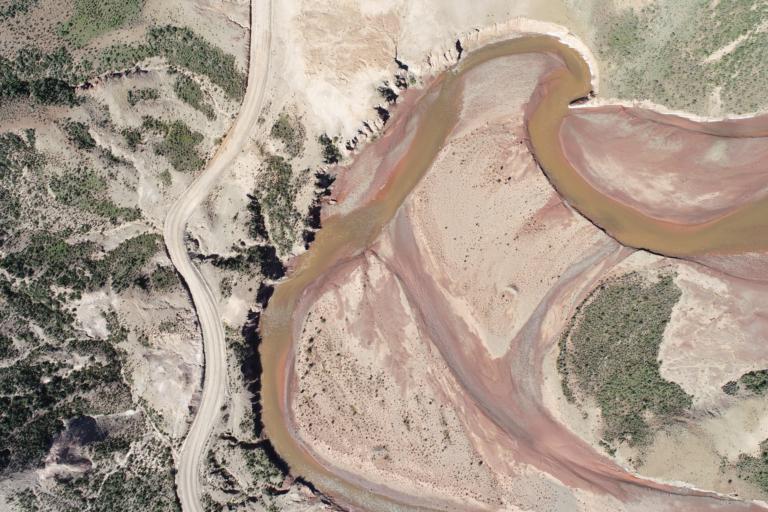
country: BO
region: La Paz
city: Curahuara de Carangas
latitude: -17.3039
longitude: -68.4911
